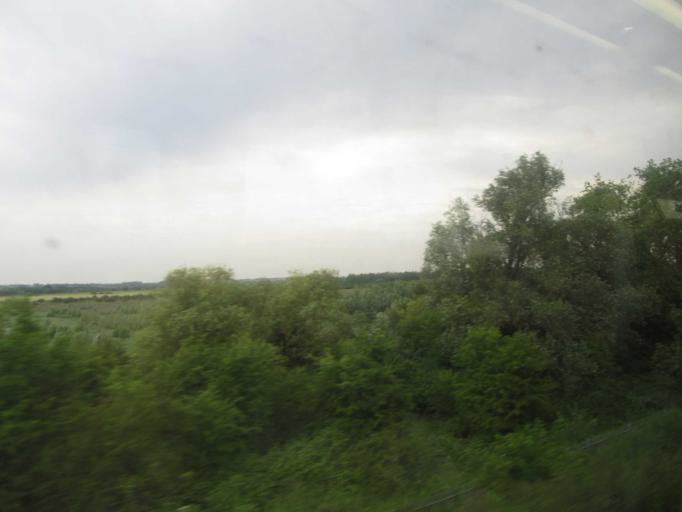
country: GB
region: England
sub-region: Bedford
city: Kempston Hardwick
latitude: 52.0735
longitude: -0.4982
